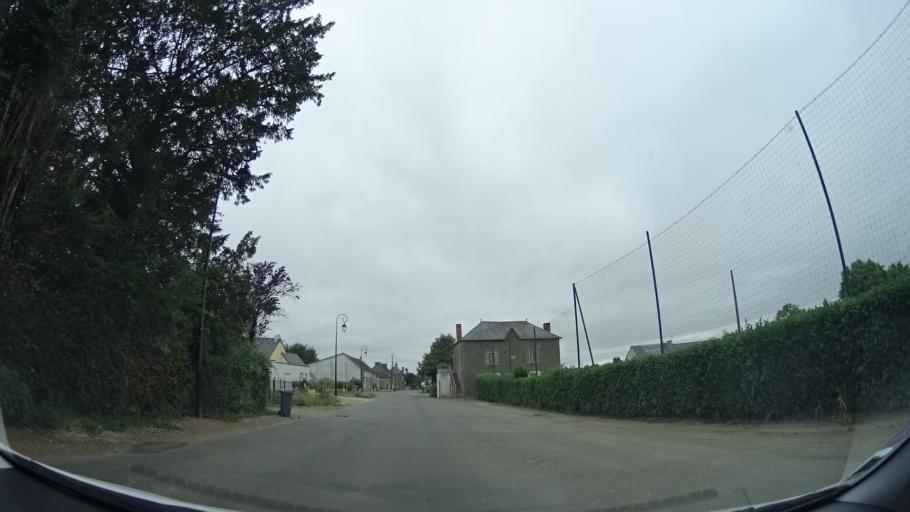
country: FR
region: Brittany
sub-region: Departement des Cotes-d'Armor
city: Evran
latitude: 48.3340
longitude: -1.9334
